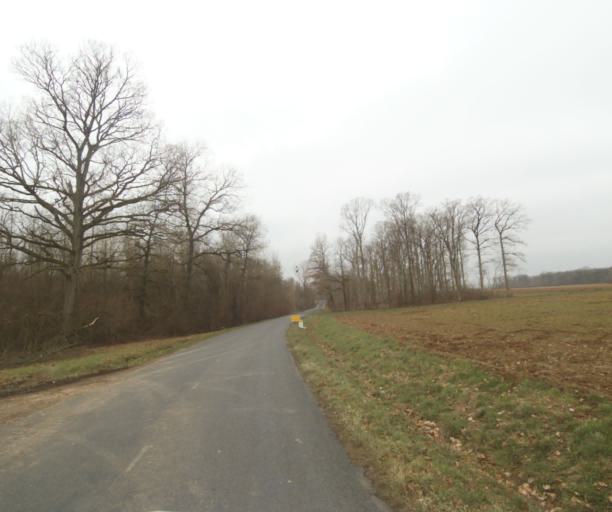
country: FR
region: Champagne-Ardenne
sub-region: Departement de la Marne
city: Pargny-sur-Saulx
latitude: 48.7359
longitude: 4.8205
